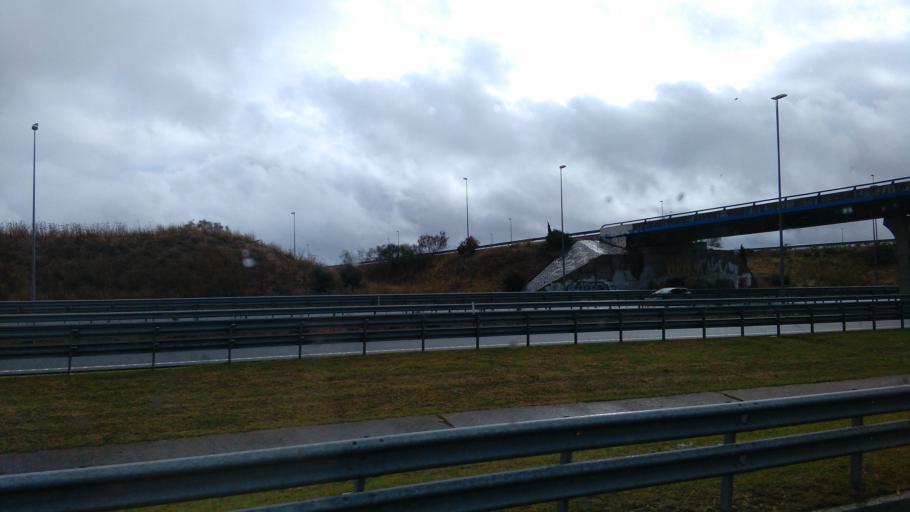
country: ES
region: Madrid
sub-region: Provincia de Madrid
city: Alcorcon
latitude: 40.3176
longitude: -3.8212
